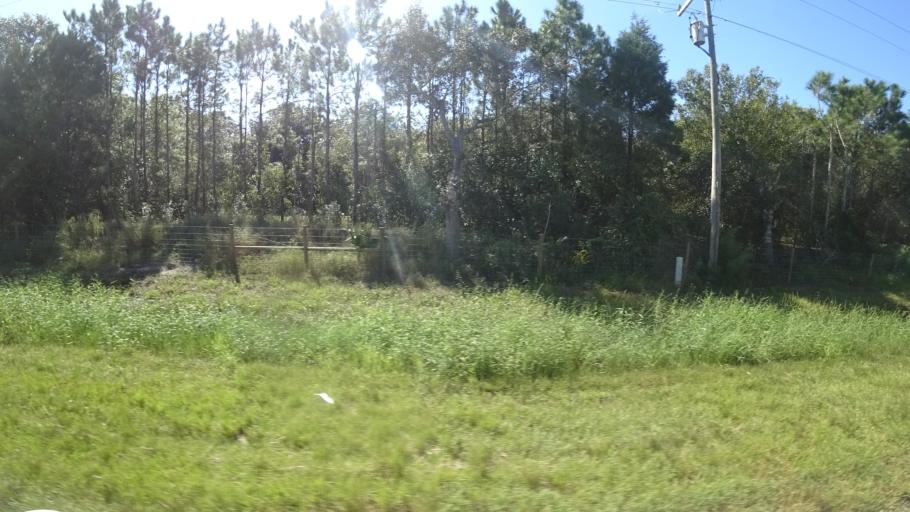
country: US
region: Florida
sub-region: Sarasota County
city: Lake Sarasota
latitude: 27.2888
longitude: -82.2316
